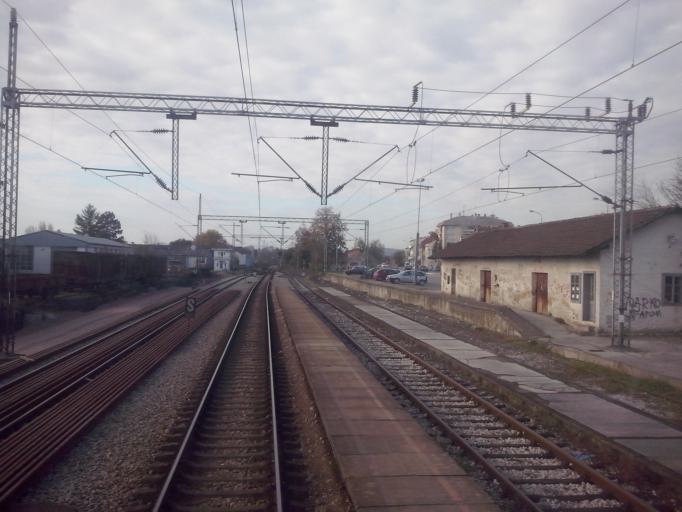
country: RS
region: Central Serbia
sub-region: Belgrade
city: Lazarevac
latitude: 44.4056
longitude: 20.2600
